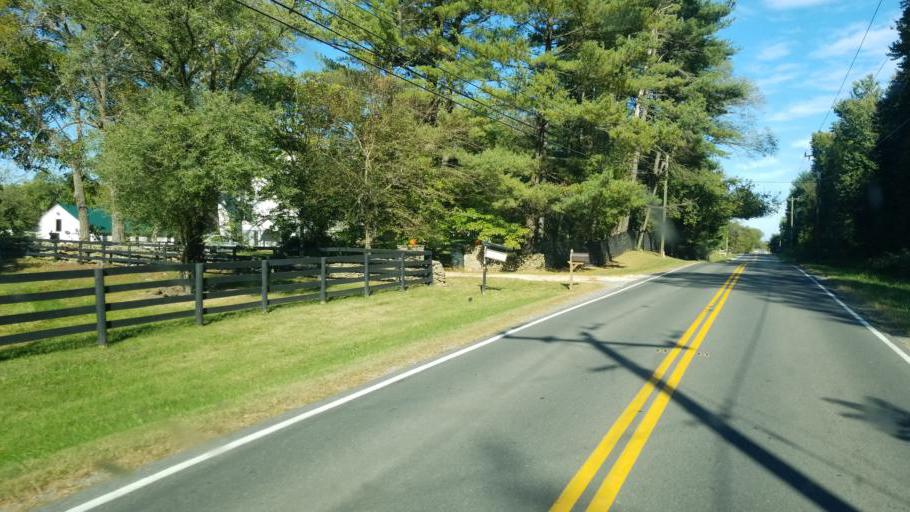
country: US
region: Virginia
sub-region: Prince William County
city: Bull Run Mountain Estates
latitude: 38.9727
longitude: -77.7150
